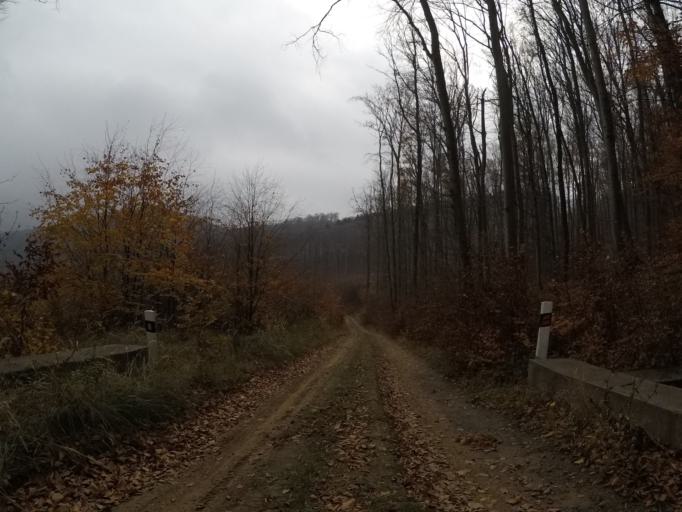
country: SK
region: Presovsky
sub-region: Okres Presov
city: Presov
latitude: 48.8860
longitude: 21.1748
